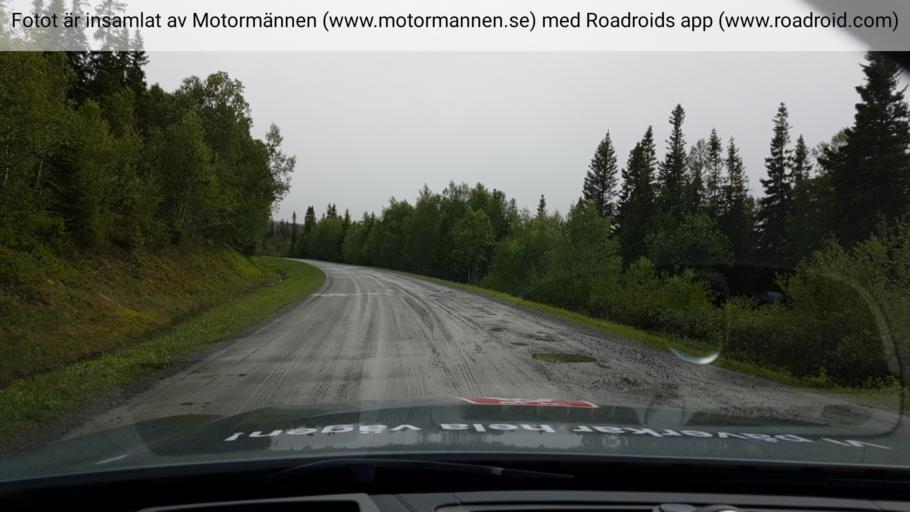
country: NO
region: Nord-Trondelag
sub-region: Snasa
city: Snaase
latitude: 63.7057
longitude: 12.3492
